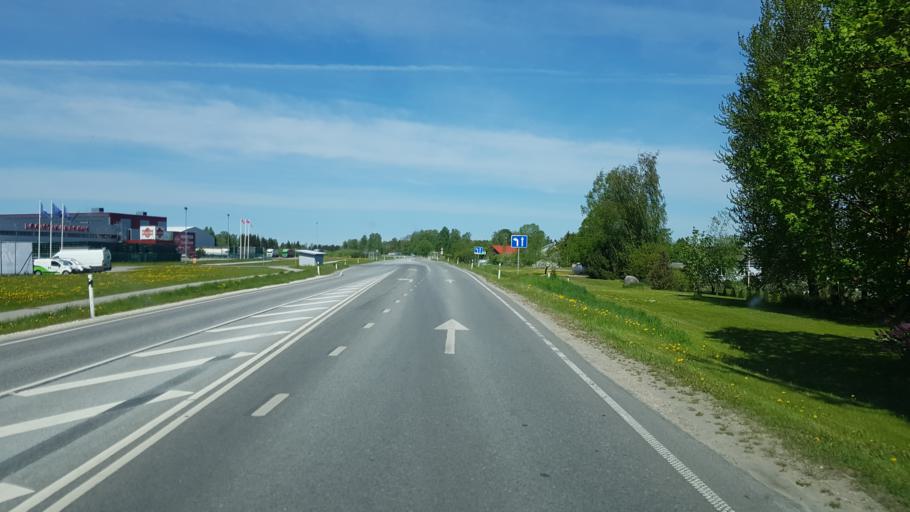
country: EE
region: Tartu
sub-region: Tartu linn
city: Tartu
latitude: 58.3983
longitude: 26.6862
